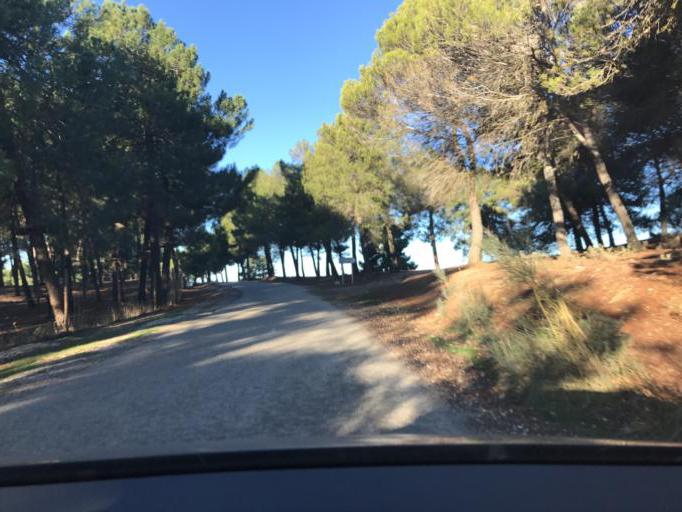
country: ES
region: Andalusia
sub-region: Provincia de Granada
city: Viznar
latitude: 37.2372
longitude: -3.5382
